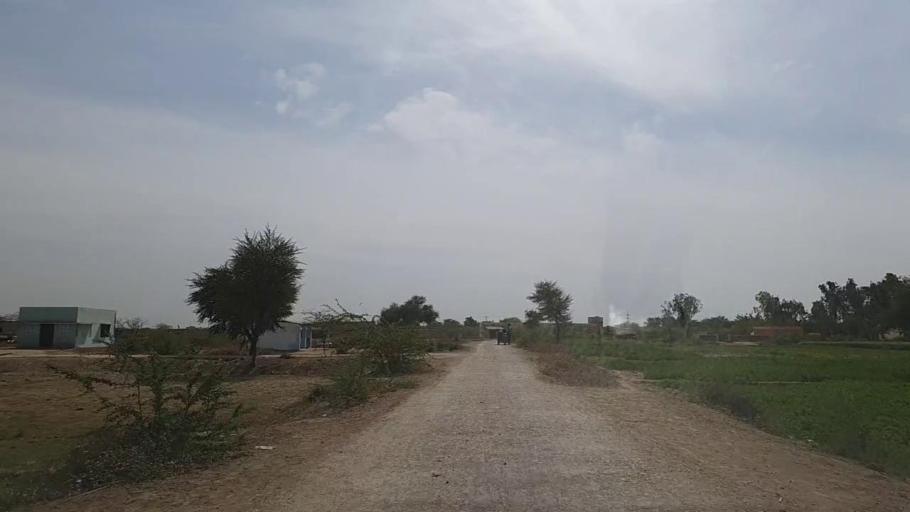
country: PK
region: Sindh
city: Samaro
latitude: 25.2100
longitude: 69.4597
